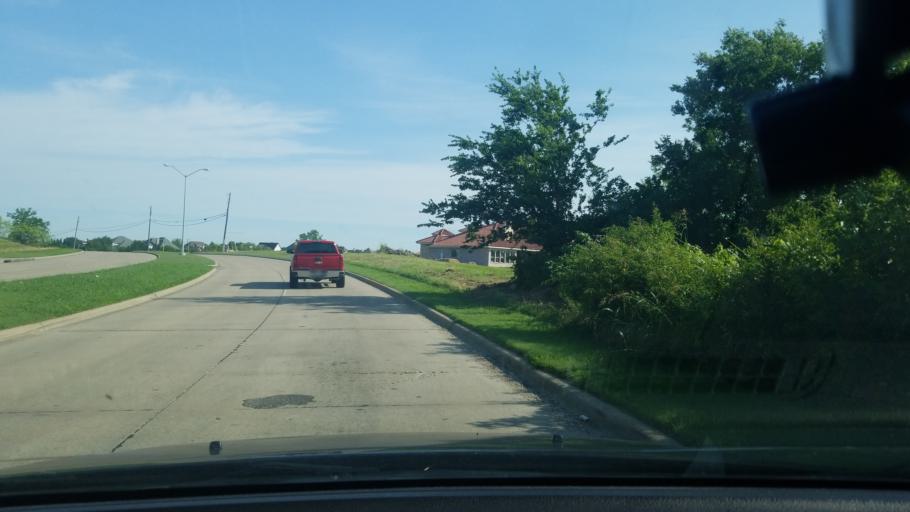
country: US
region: Texas
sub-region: Dallas County
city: Sunnyvale
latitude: 32.7760
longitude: -96.5616
